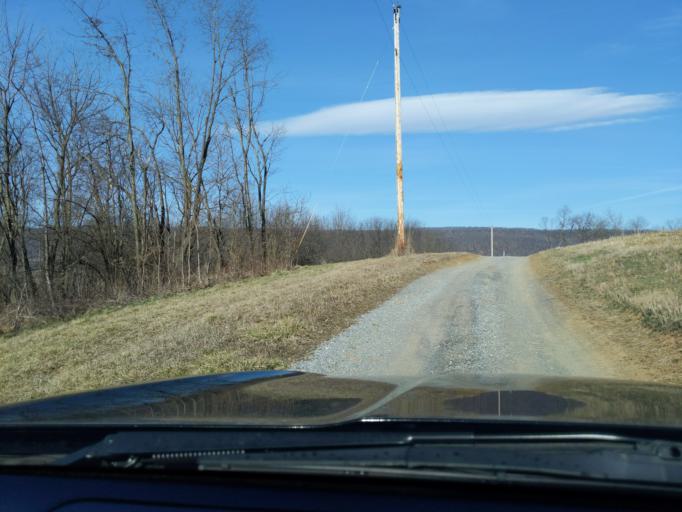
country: US
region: Pennsylvania
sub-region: Blair County
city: Martinsburg
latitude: 40.3901
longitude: -78.2688
